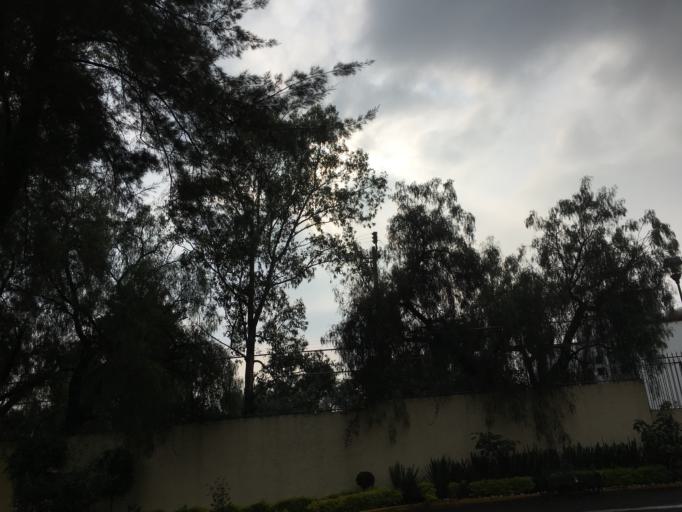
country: MX
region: Mexico City
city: Tlalpan
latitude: 19.2810
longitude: -99.1457
